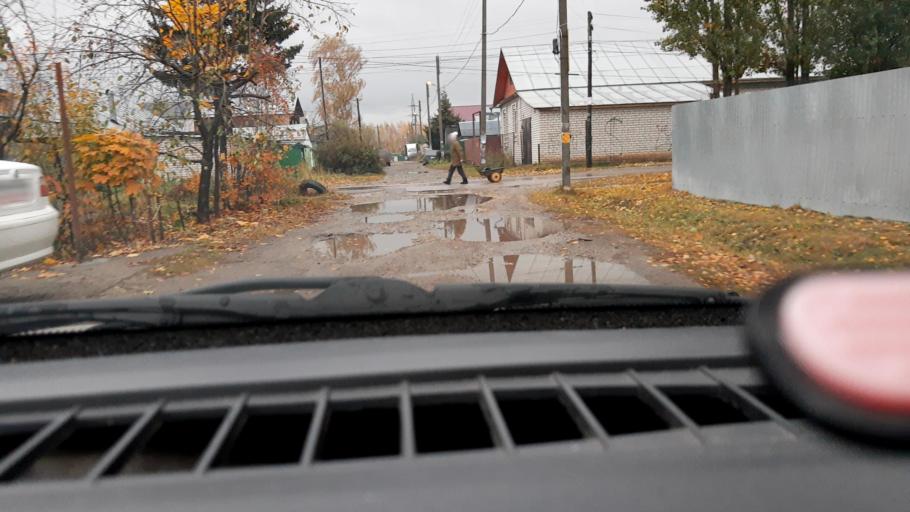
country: RU
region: Nizjnij Novgorod
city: Nizhniy Novgorod
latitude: 56.2838
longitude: 43.8991
